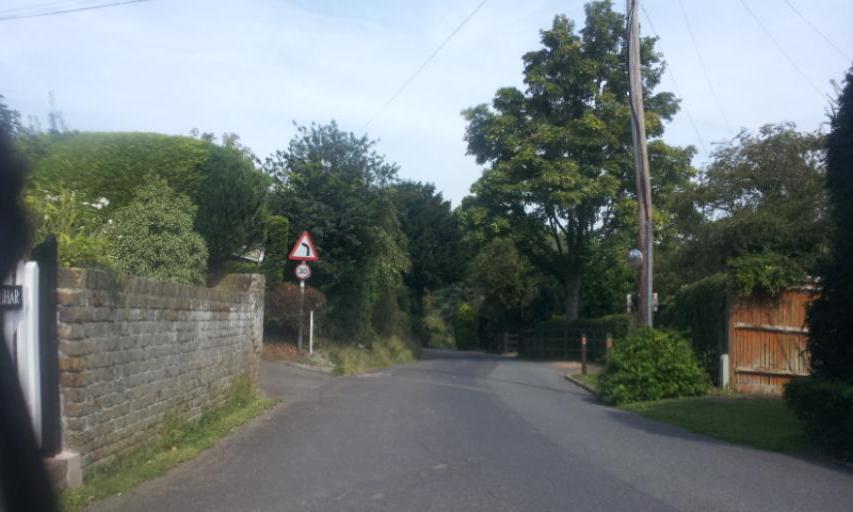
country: GB
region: England
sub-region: Kent
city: Newington
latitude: 51.3459
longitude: 0.6388
